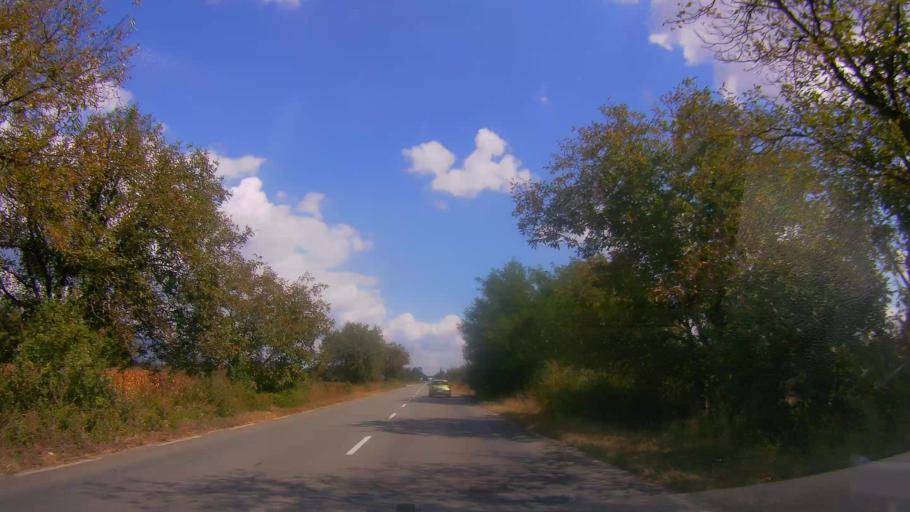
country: BG
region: Sliven
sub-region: Obshtina Tvurditsa
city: Tvurditsa
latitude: 42.6562
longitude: 25.8874
